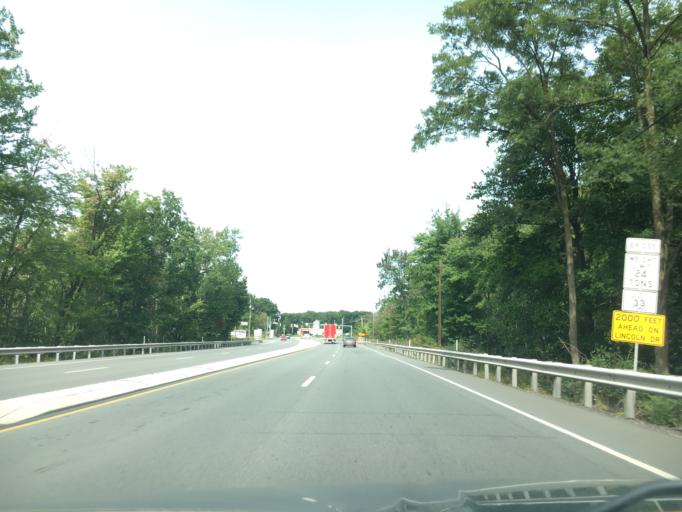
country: US
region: Pennsylvania
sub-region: Schuylkill County
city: Hometown
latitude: 40.8313
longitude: -75.9869
